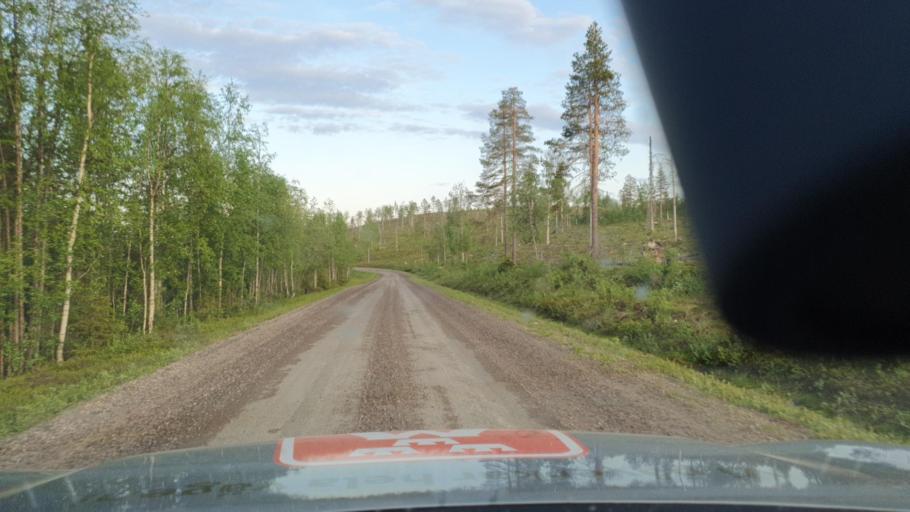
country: SE
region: Norrbotten
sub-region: Bodens Kommun
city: Boden
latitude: 66.4813
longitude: 21.6092
